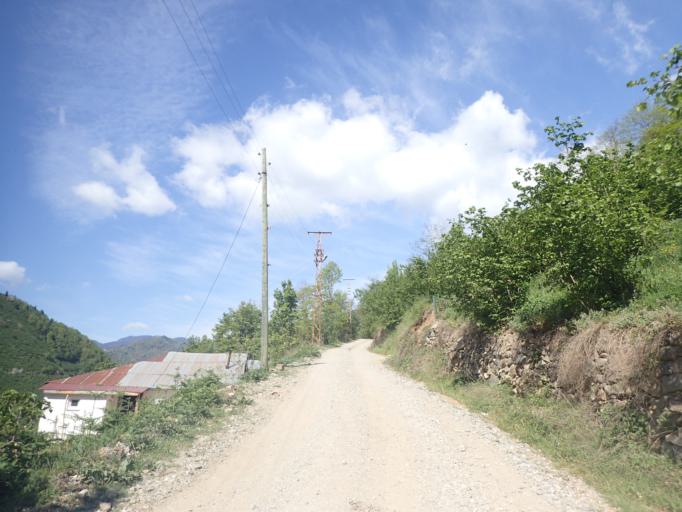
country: TR
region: Ordu
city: Topcam
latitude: 40.7139
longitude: 37.8778
